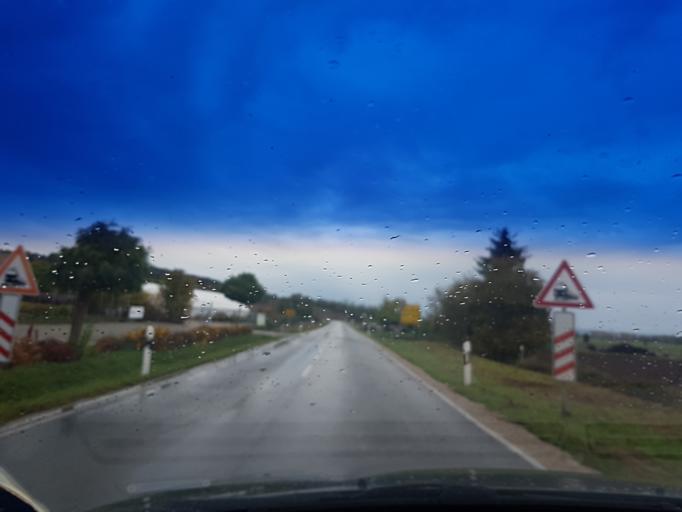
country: DE
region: Bavaria
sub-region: Regierungsbezirk Mittelfranken
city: Muhlhausen
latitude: 49.7569
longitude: 10.7831
